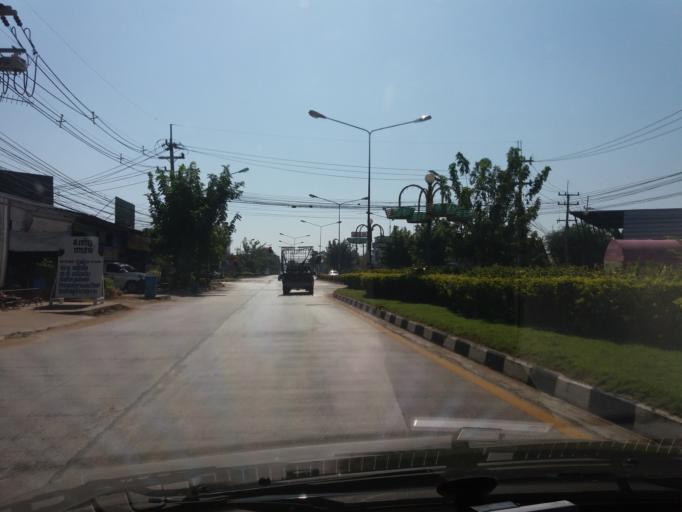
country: TH
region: Kamphaeng Phet
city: Khanu Woralaksaburi
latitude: 16.0711
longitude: 99.8621
